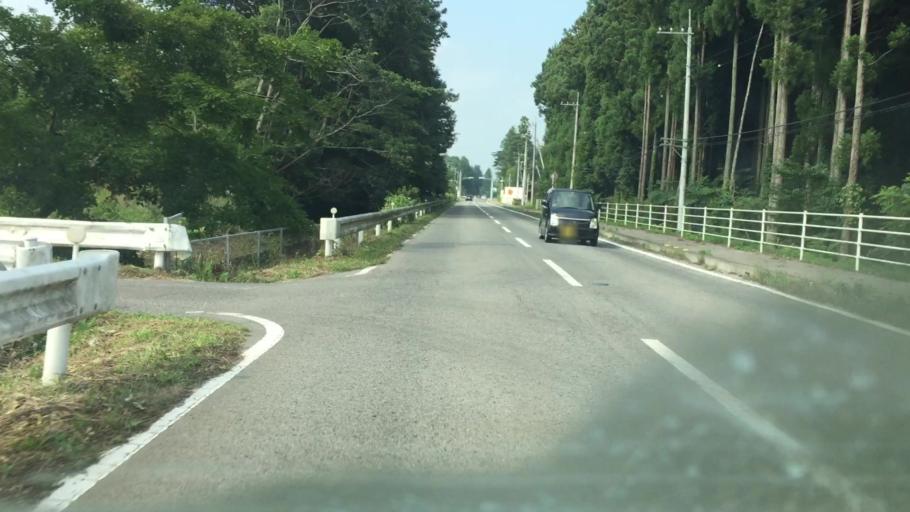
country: JP
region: Tochigi
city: Kuroiso
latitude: 36.9834
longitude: 139.9846
